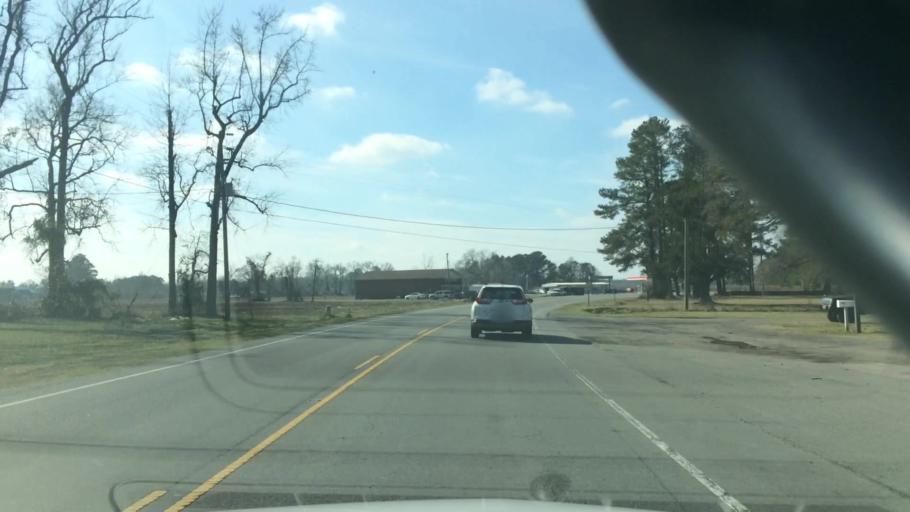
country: US
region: North Carolina
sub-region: Duplin County
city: Beulaville
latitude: 34.8300
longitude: -77.8088
